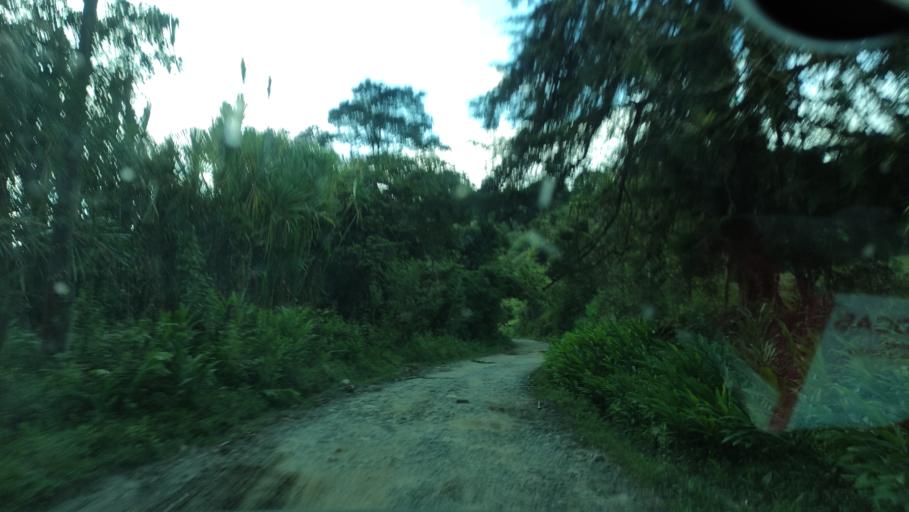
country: CO
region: Valle del Cauca
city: Buga
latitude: 3.8818
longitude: -76.1804
